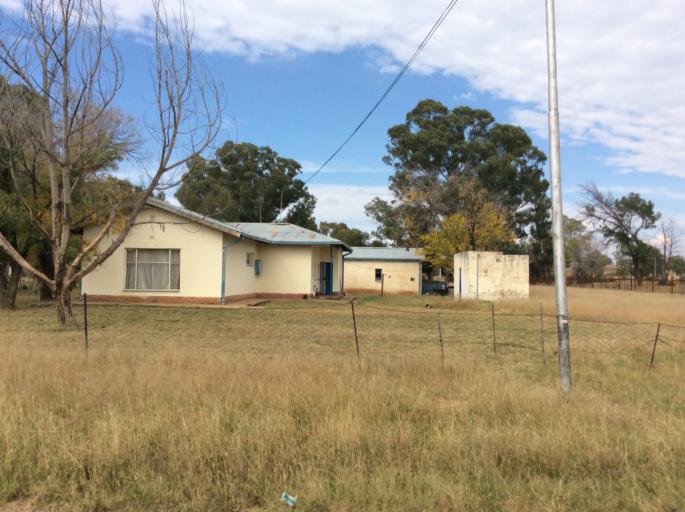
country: LS
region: Mafeteng
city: Mafeteng
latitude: -29.7301
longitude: 27.0276
